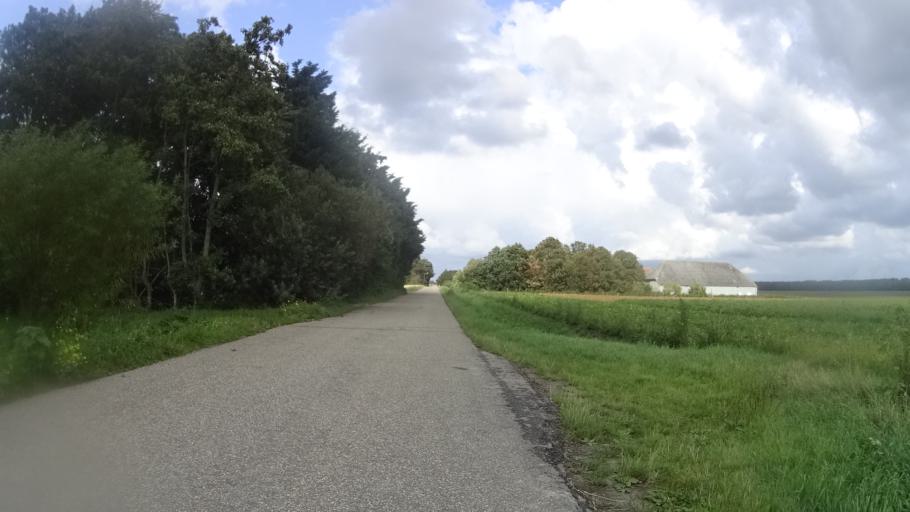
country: NL
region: North Holland
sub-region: Gemeente Schagen
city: Schagen
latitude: 52.8511
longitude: 4.8823
